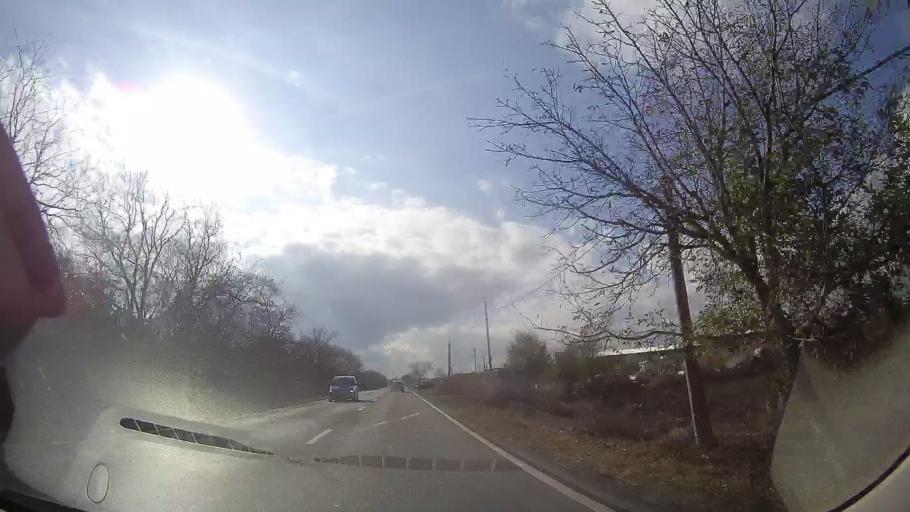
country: RO
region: Constanta
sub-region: Comuna Agigea
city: Agigea
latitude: 44.0832
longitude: 28.6058
